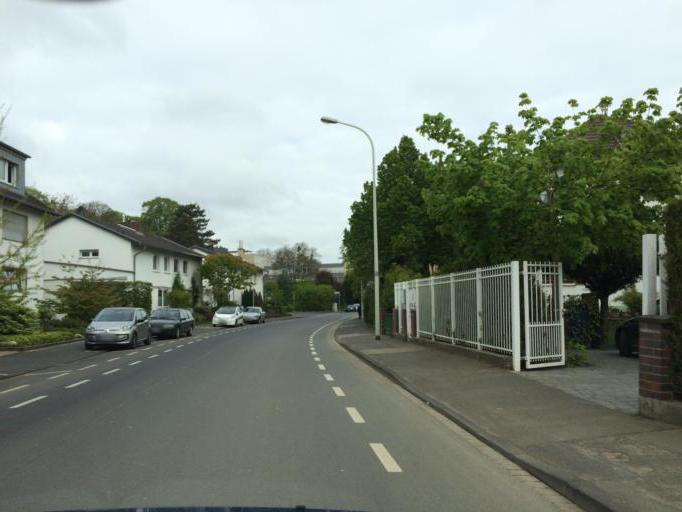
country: DE
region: North Rhine-Westphalia
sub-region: Regierungsbezirk Koln
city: Konigswinter
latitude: 50.6740
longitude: 7.1618
